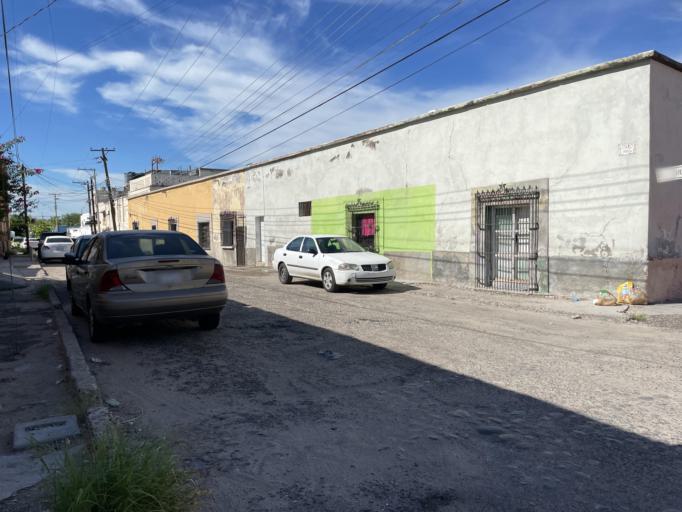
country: MX
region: Sonora
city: Hermosillo
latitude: 29.0746
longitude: -110.9553
